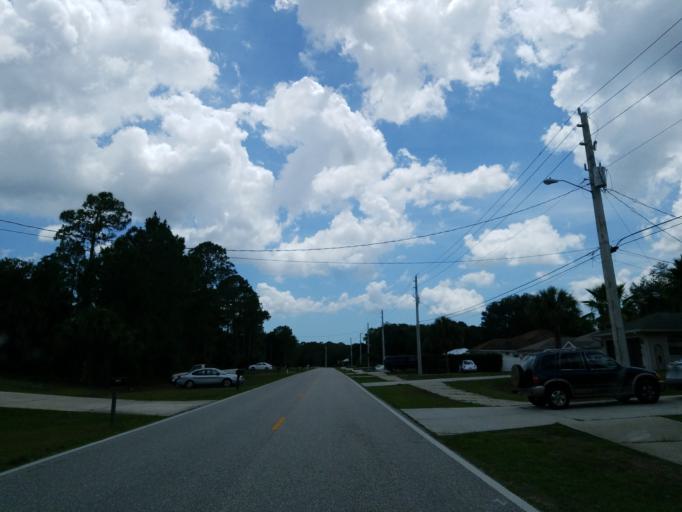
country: US
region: Florida
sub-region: Sarasota County
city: North Port
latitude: 27.0850
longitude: -82.1818
